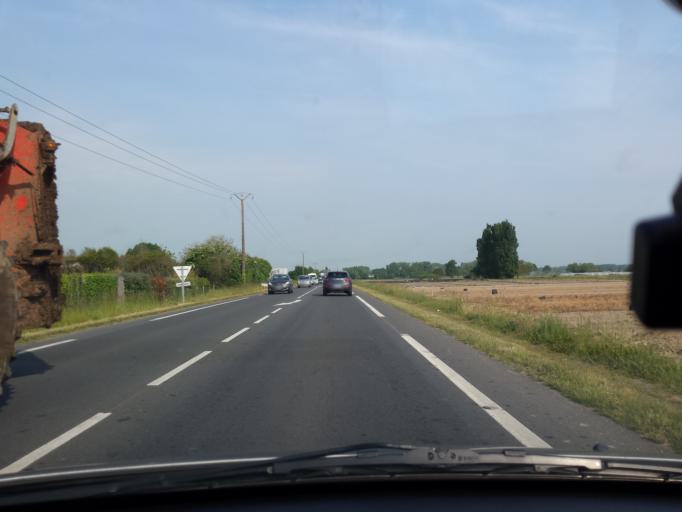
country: FR
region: Pays de la Loire
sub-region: Departement de la Loire-Atlantique
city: Machecoul
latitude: 46.9909
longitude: -1.7983
